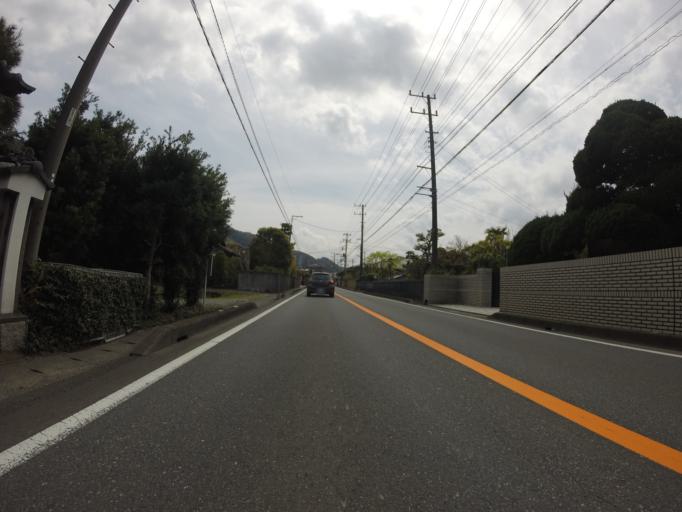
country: JP
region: Shizuoka
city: Numazu
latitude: 35.0704
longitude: 138.8759
